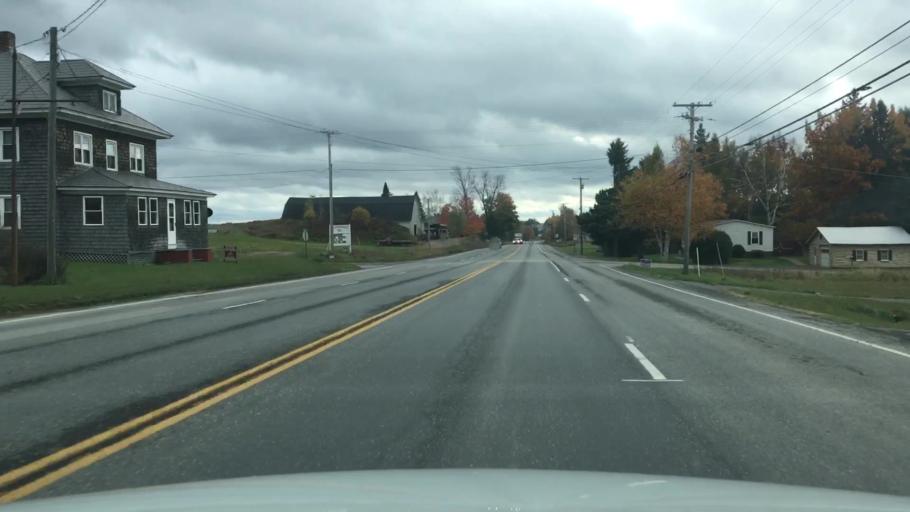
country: US
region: Maine
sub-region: Aroostook County
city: Houlton
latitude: 46.2177
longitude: -67.8410
